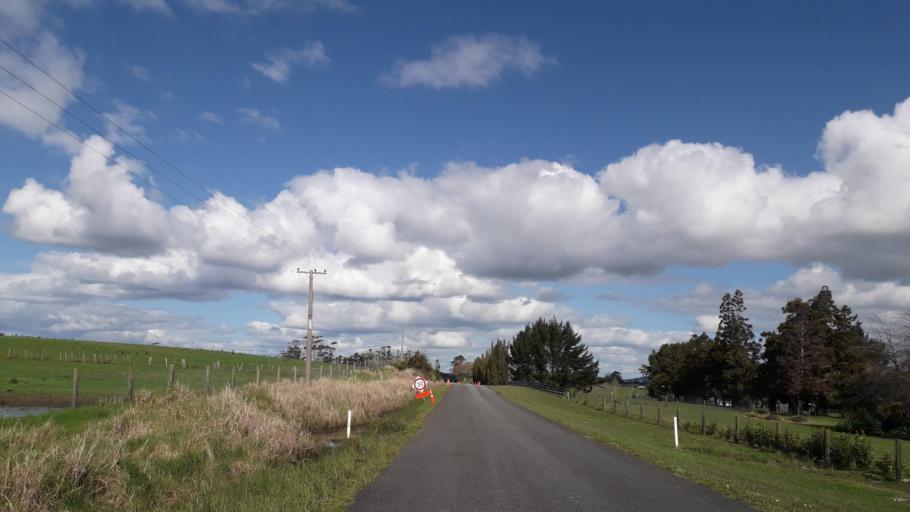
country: NZ
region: Northland
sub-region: Far North District
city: Kerikeri
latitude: -35.1793
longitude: 173.9331
